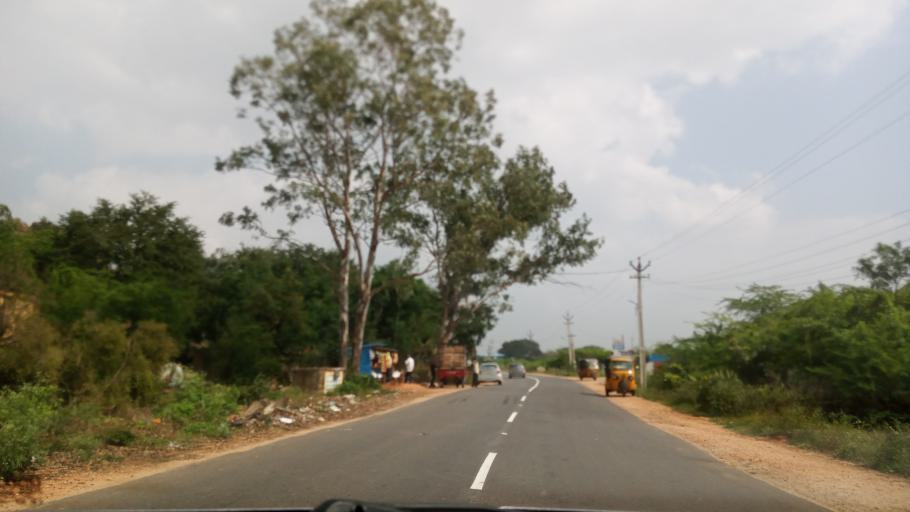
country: IN
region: Andhra Pradesh
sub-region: Chittoor
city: Madanapalle
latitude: 13.6340
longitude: 78.6186
